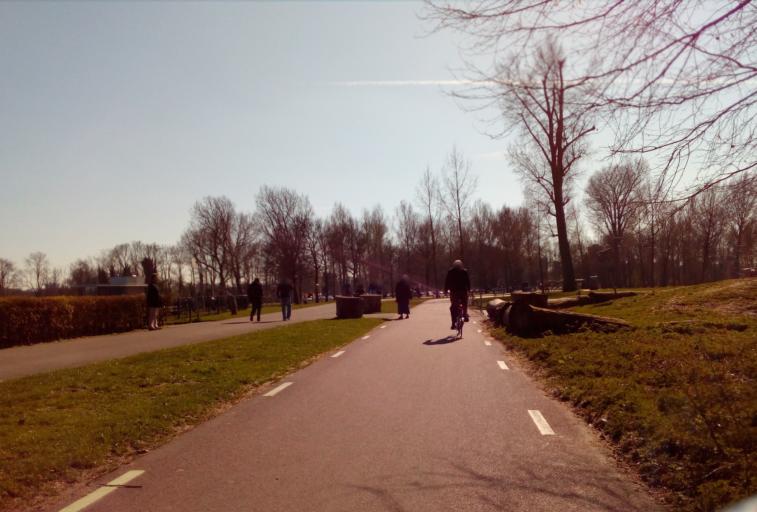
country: NL
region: South Holland
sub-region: Gemeente Rotterdam
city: Rotterdam
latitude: 51.9389
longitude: 4.5069
